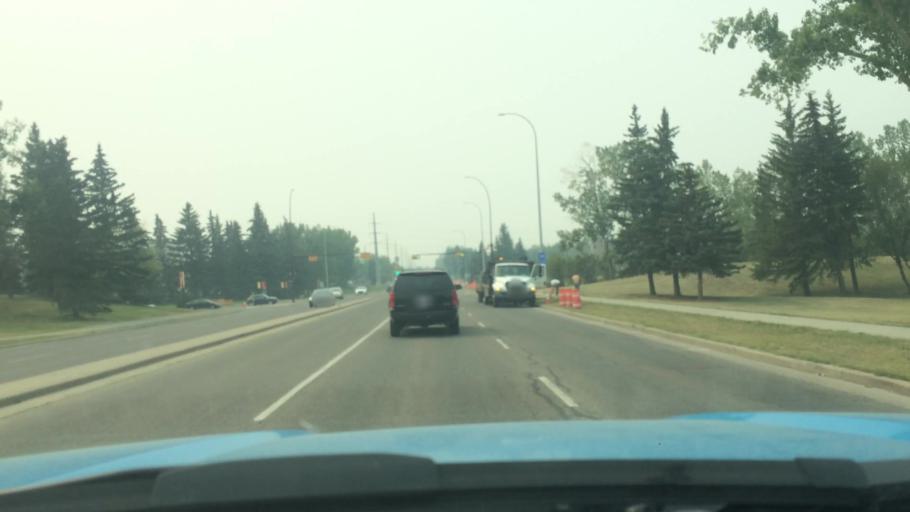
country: CA
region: Alberta
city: Calgary
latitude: 51.0816
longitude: -114.1358
